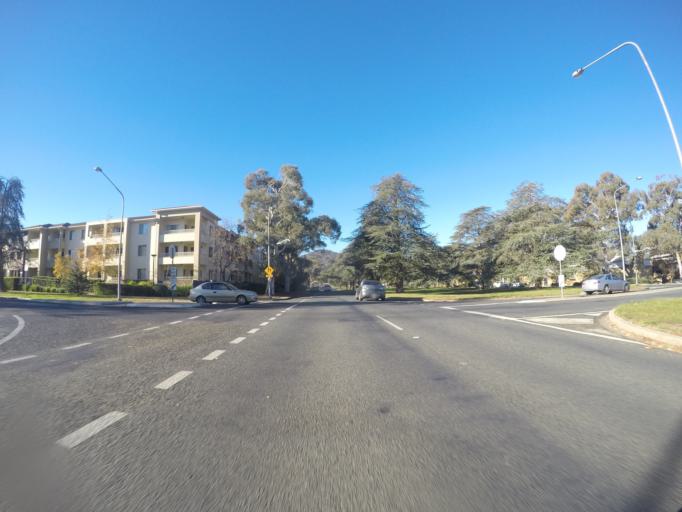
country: AU
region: Australian Capital Territory
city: Canberra
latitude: -35.2780
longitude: 149.1385
